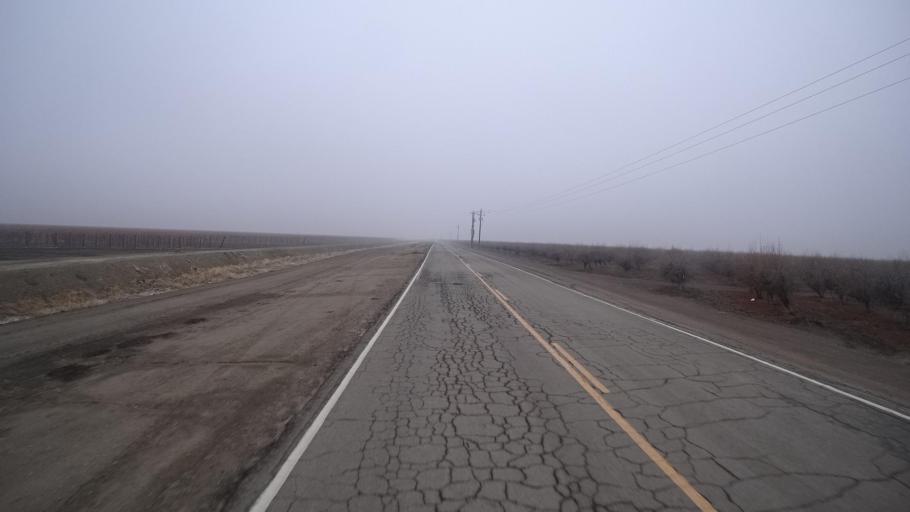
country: US
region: California
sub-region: Kern County
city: Lost Hills
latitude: 35.5121
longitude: -119.6142
